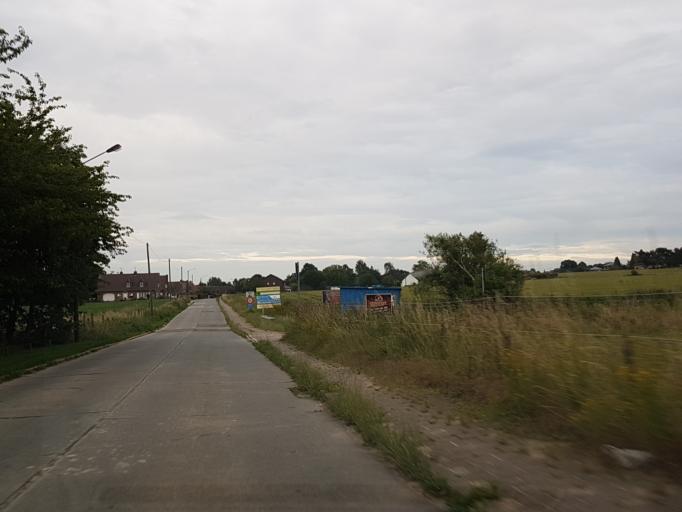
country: BE
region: Flanders
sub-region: Provincie Vlaams-Brabant
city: Bever
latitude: 50.9384
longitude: 4.2940
